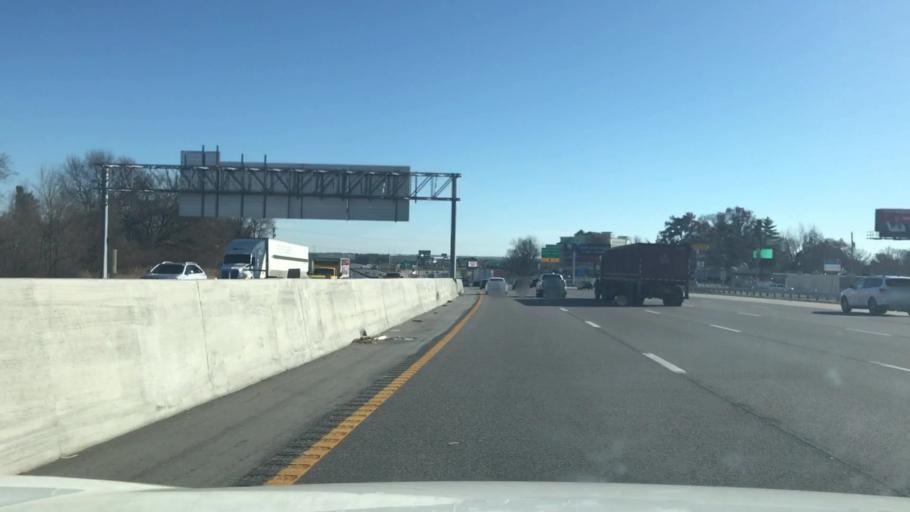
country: US
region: Missouri
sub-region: Saint Charles County
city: Saint Charles
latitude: 38.7747
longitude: -90.5088
